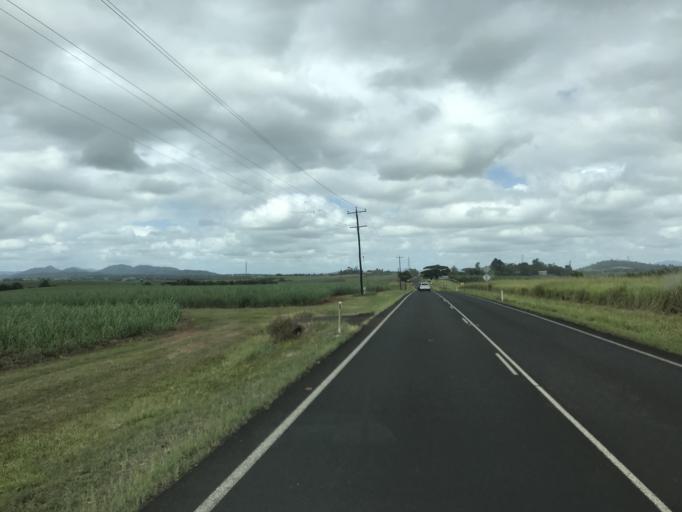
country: AU
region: Queensland
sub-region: Cassowary Coast
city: Innisfail
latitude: -17.5804
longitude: 145.9983
